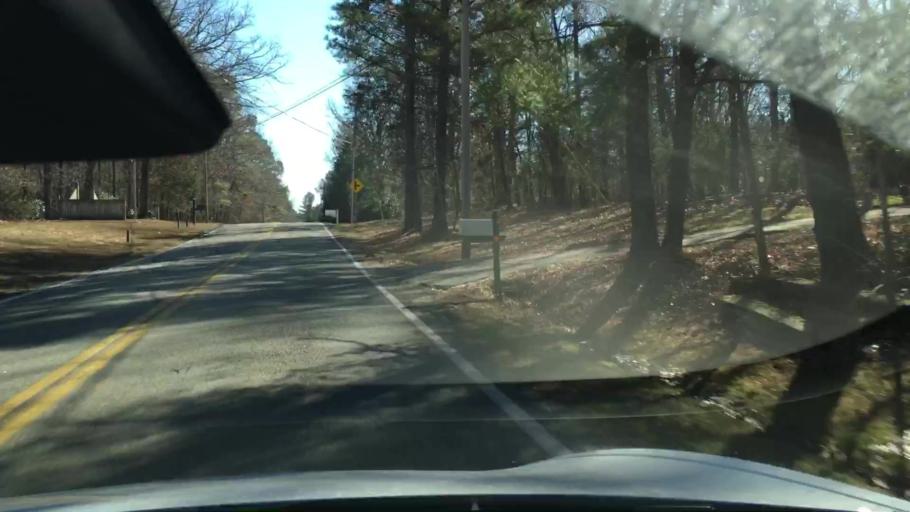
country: US
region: Virginia
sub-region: Henrico County
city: Short Pump
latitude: 37.5740
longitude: -77.7198
